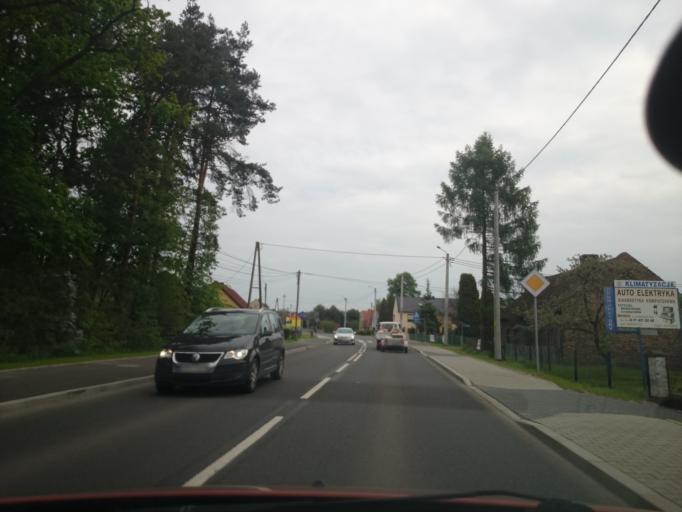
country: PL
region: Opole Voivodeship
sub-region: Powiat opolski
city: Kup
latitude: 50.8144
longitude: 17.8832
